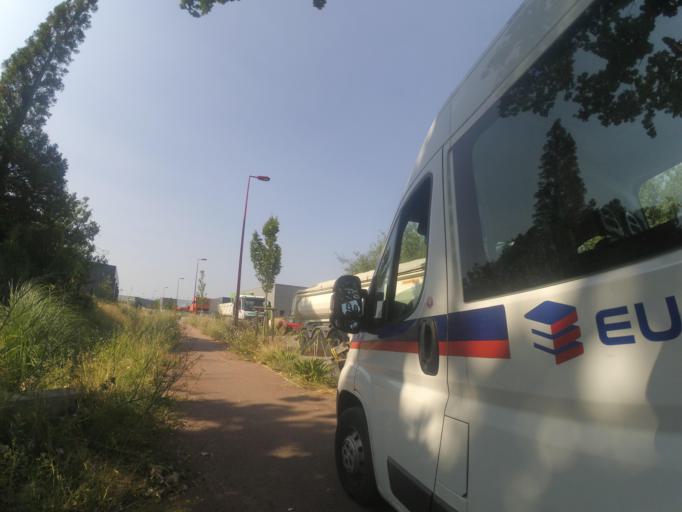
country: FR
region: Languedoc-Roussillon
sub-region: Departement des Pyrenees-Orientales
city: Toulouges
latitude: 42.6647
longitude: 2.8213
